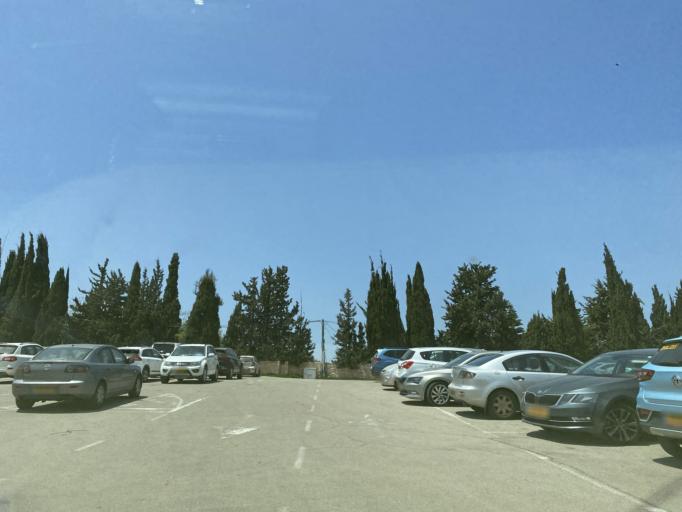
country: IL
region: Tel Aviv
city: Ramat HaSharon
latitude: 32.1295
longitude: 34.8278
